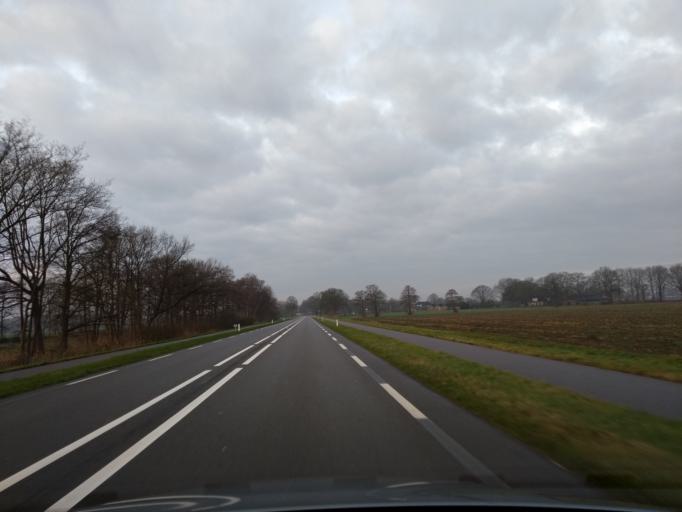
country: NL
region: Gelderland
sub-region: Gemeente Lochem
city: Laren
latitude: 52.2766
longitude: 6.3662
